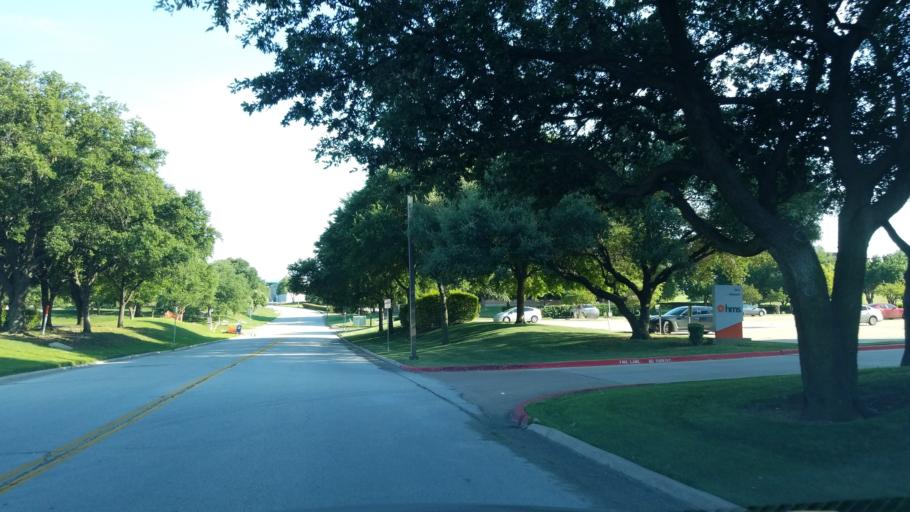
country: US
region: Texas
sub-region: Dallas County
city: Irving
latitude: 32.8884
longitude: -96.9715
